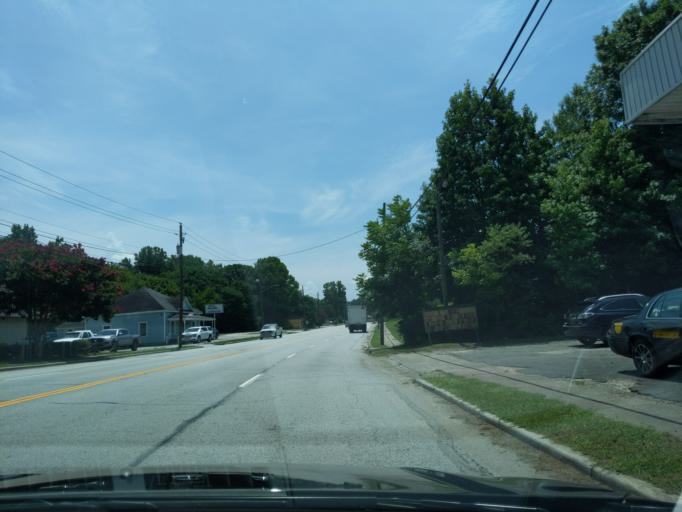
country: US
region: South Carolina
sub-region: Laurens County
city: Laurens
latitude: 34.5045
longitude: -82.0216
